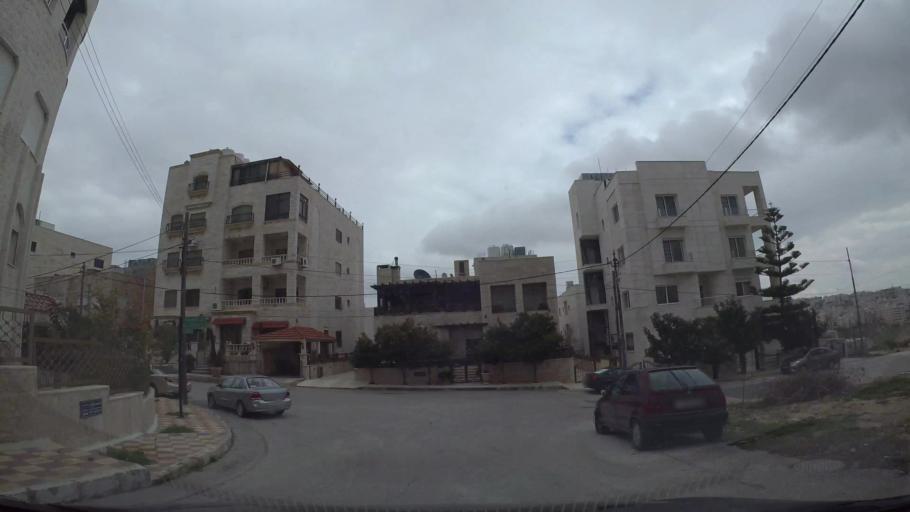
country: JO
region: Amman
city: Wadi as Sir
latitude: 31.9649
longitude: 35.8297
